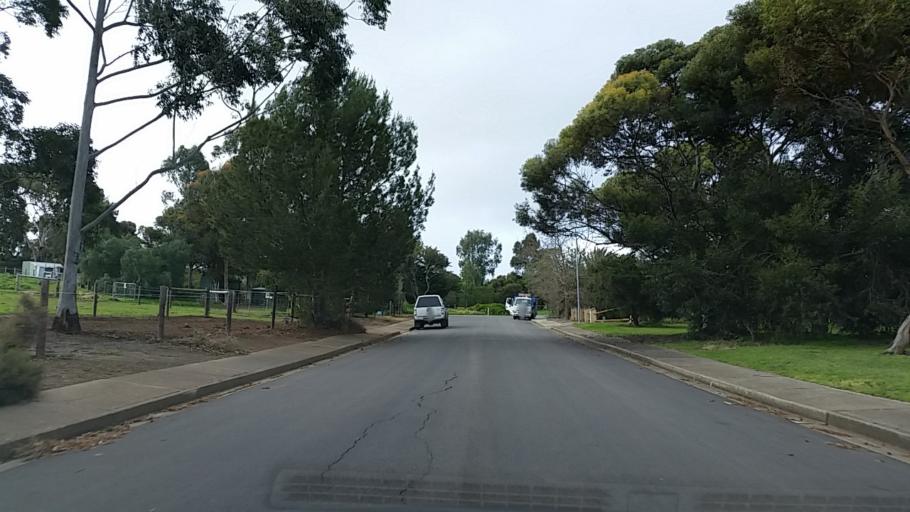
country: AU
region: South Australia
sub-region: Marion
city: Trott Park
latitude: -35.0639
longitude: 138.5381
